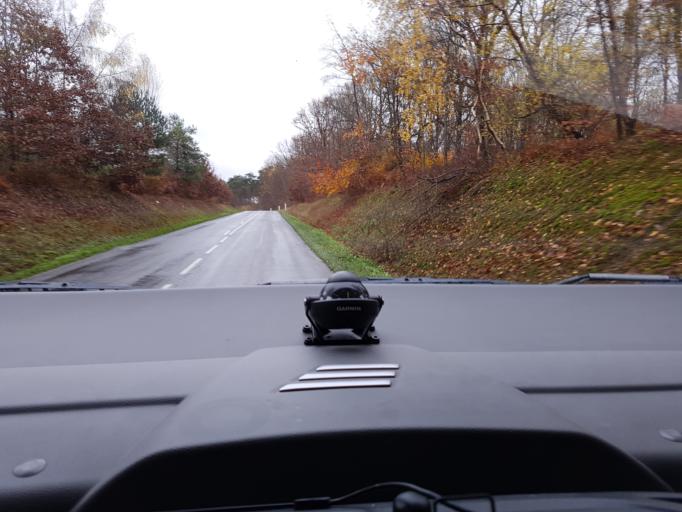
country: FR
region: Haute-Normandie
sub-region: Departement de l'Eure
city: Pont-Saint-Pierre
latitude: 49.3234
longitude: 1.2934
